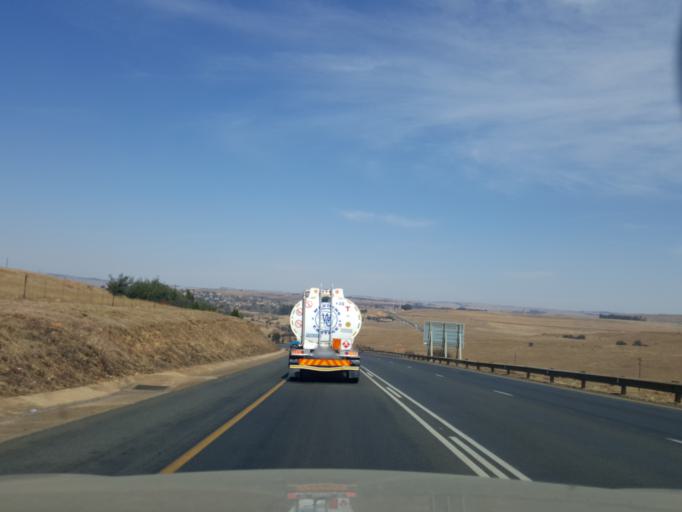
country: ZA
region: Mpumalanga
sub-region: Nkangala District Municipality
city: Belfast
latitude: -25.6355
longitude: 30.2533
